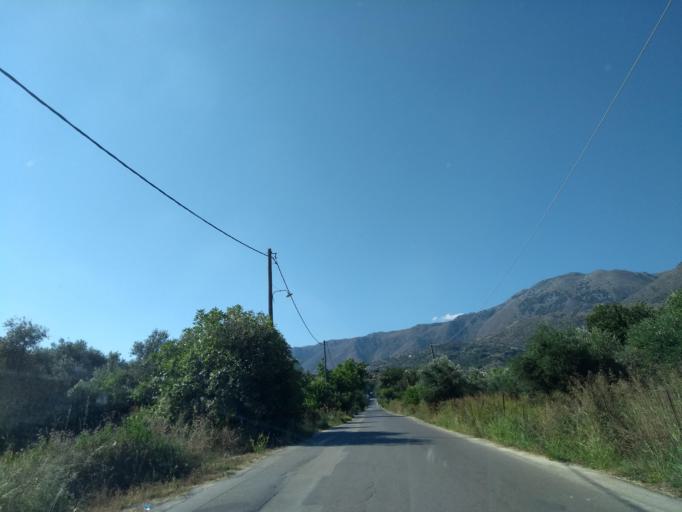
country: GR
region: Crete
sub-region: Nomos Chanias
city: Georgioupolis
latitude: 35.3372
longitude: 24.2794
